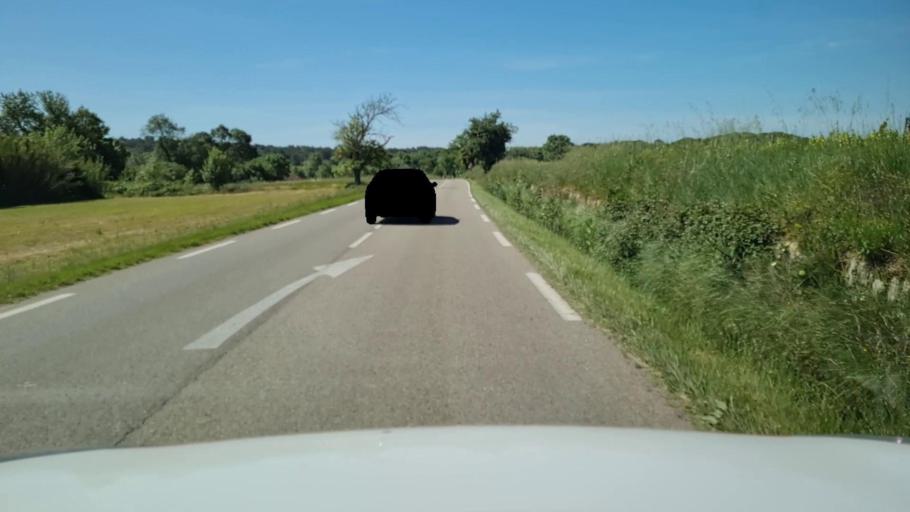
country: FR
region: Languedoc-Roussillon
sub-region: Departement du Gard
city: Villevieille
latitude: 43.8164
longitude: 4.0955
